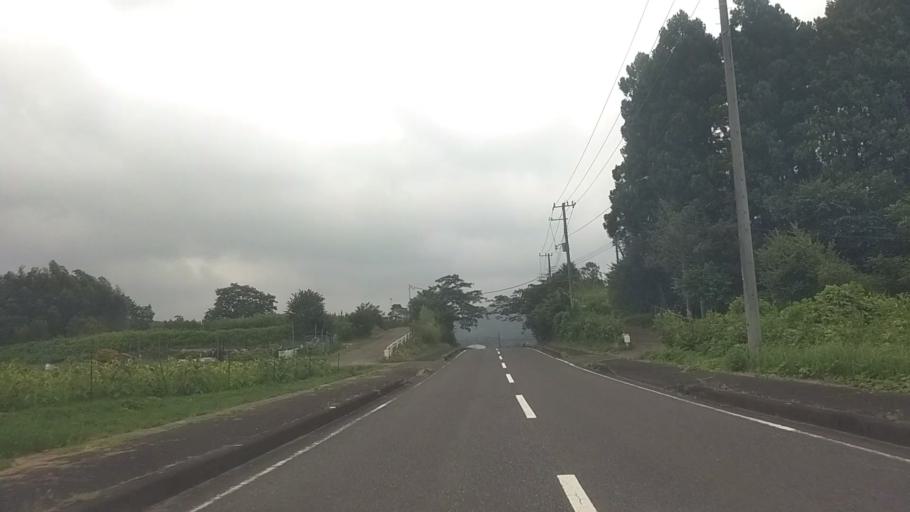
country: JP
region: Chiba
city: Kawaguchi
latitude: 35.2349
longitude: 140.0857
